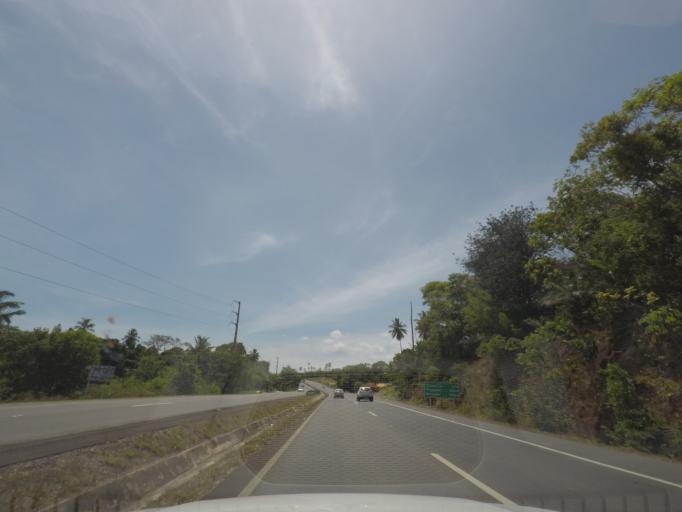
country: BR
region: Bahia
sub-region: Mata De Sao Joao
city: Mata de Sao Joao
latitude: -12.5694
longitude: -38.0340
